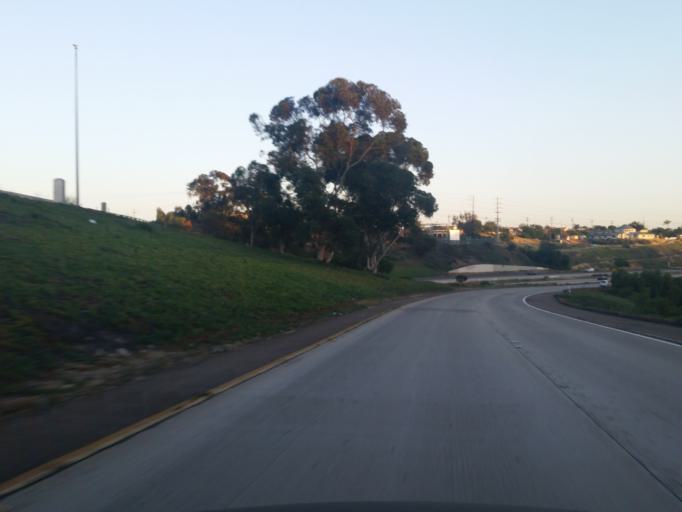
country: US
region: California
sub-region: San Diego County
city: San Diego
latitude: 32.7326
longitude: -117.1127
